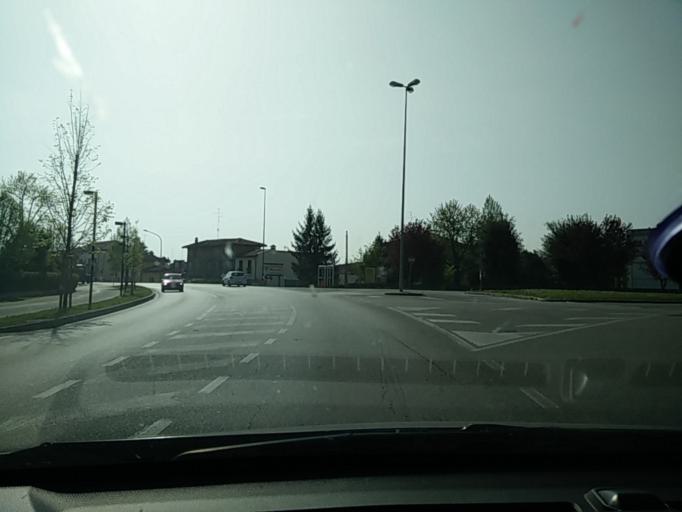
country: IT
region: Friuli Venezia Giulia
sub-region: Provincia di Pordenone
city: Pordenone
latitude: 45.9490
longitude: 12.6754
